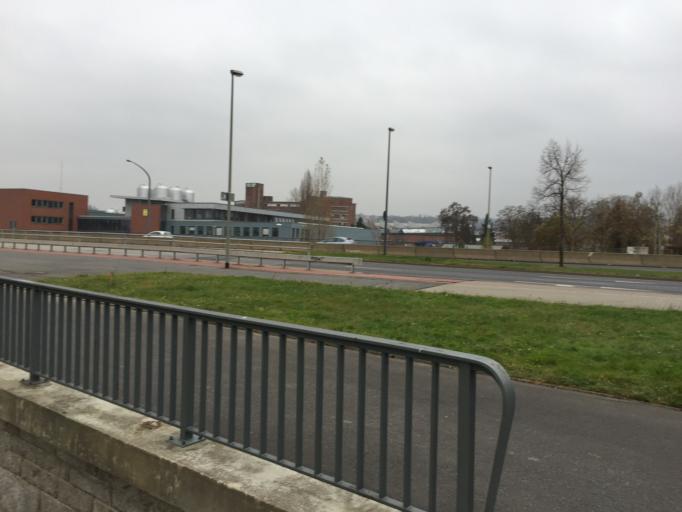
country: DE
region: Saxony
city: Dresden
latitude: 51.0416
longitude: 13.7084
